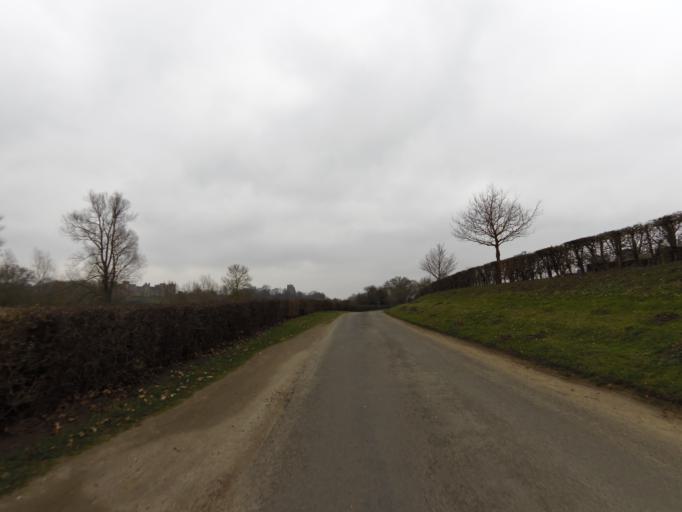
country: GB
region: England
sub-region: Suffolk
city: Framlingham
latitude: 52.2281
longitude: 1.3426
